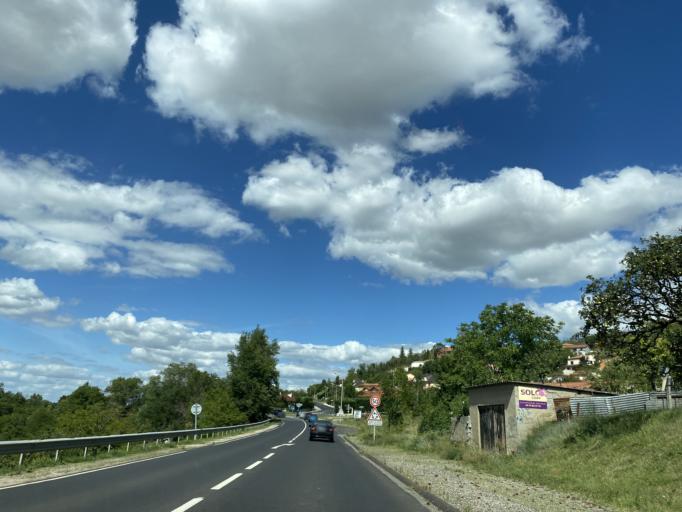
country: FR
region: Auvergne
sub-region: Departement du Puy-de-Dome
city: Dallet
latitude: 45.7643
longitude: 3.2373
